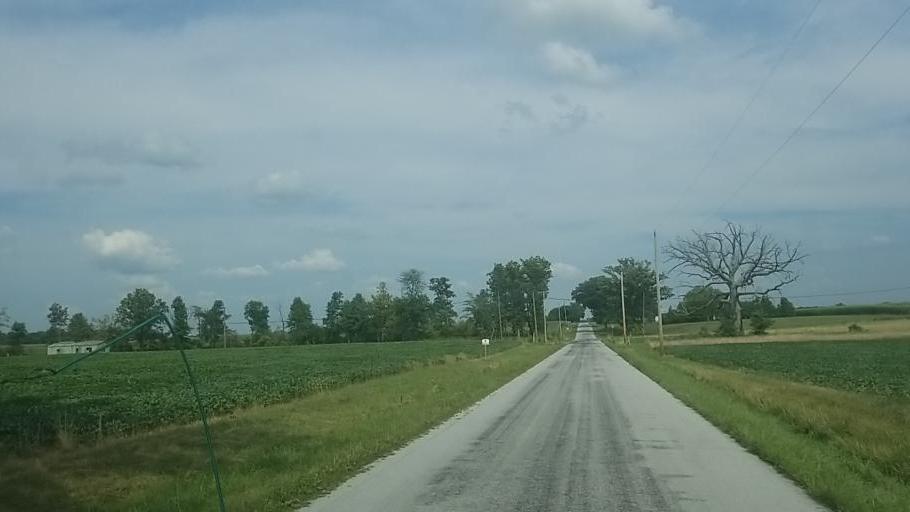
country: US
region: Ohio
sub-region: Hardin County
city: Forest
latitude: 40.8176
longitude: -83.4014
